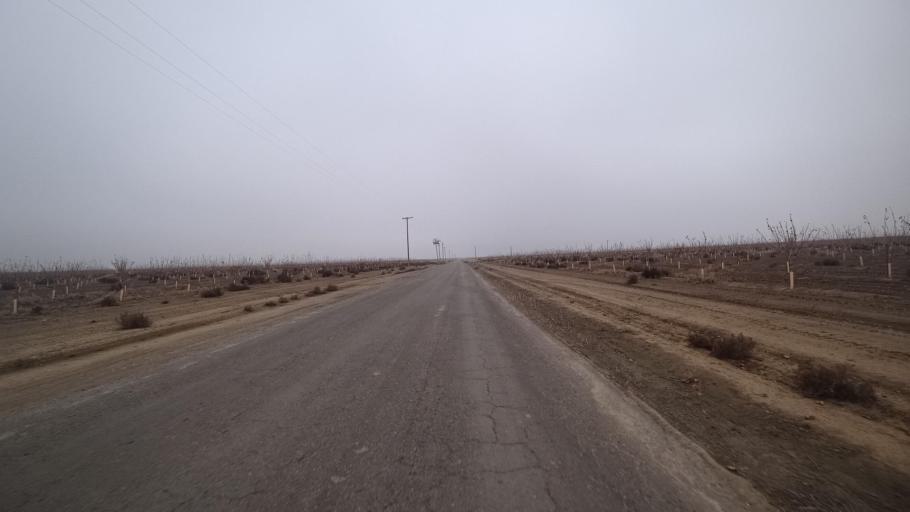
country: US
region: California
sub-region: Kern County
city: Wasco
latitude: 35.6980
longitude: -119.4195
